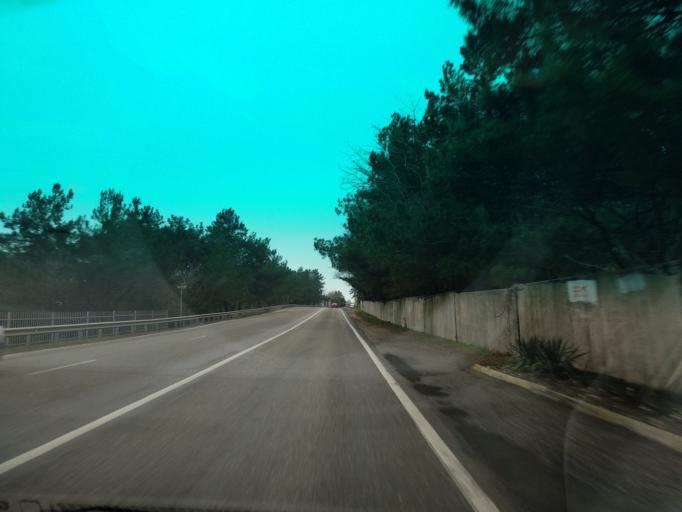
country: RU
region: Krasnodarskiy
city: Ol'ginka
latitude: 44.1875
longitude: 38.9057
